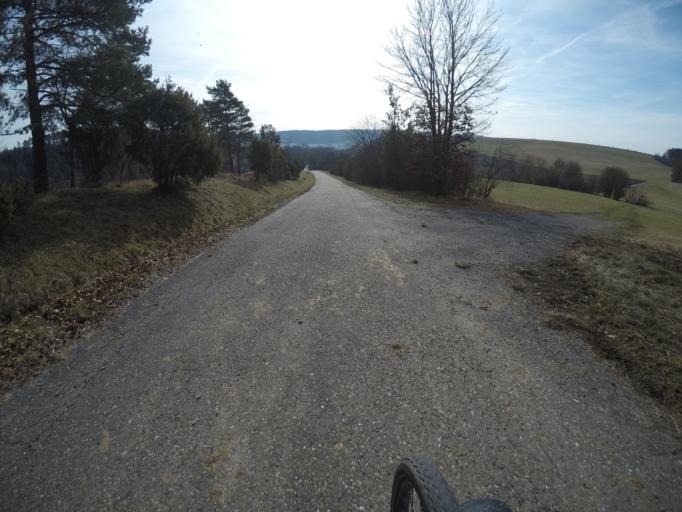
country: DE
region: Baden-Wuerttemberg
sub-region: Karlsruhe Region
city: Wildberg
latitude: 48.6623
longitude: 8.7716
